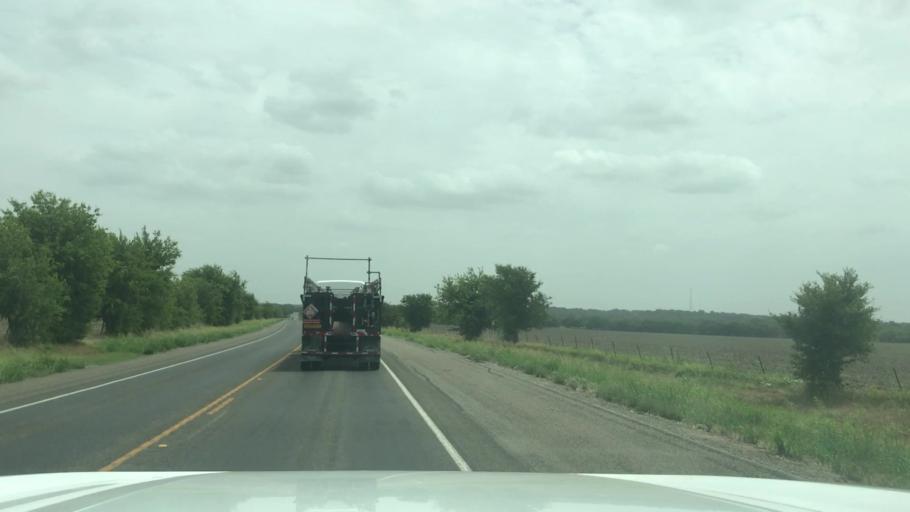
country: US
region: Texas
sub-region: Bosque County
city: Valley Mills
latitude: 31.6658
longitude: -97.4939
